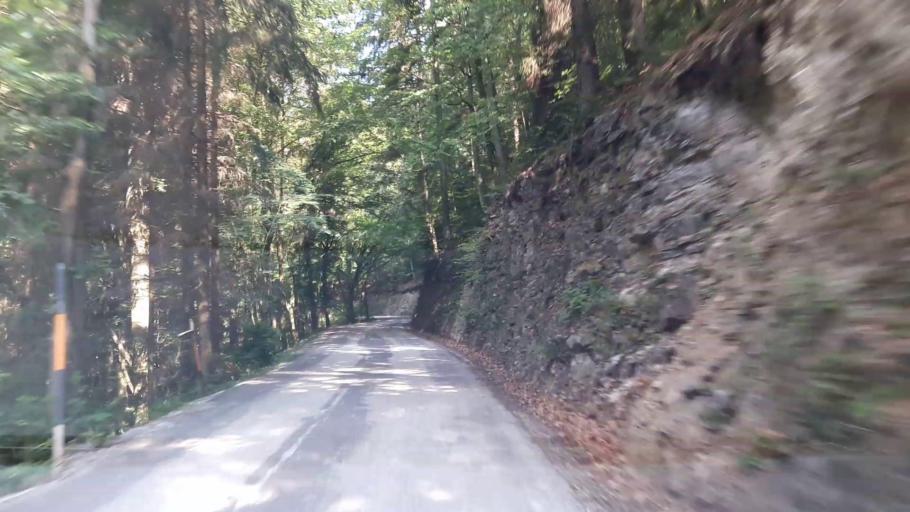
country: AT
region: Lower Austria
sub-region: Politischer Bezirk Krems
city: Aggsbach
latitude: 48.2881
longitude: 15.3772
